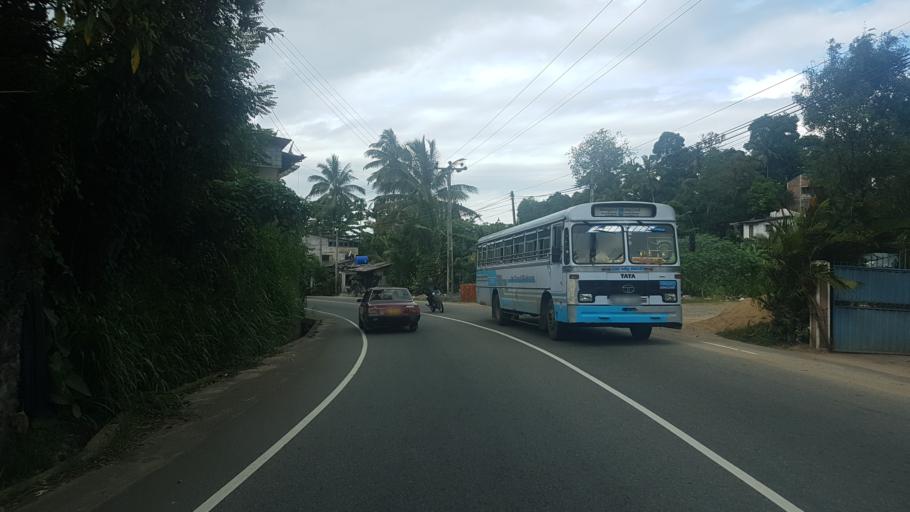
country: LK
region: Central
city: Kandy
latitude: 7.2385
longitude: 80.5938
